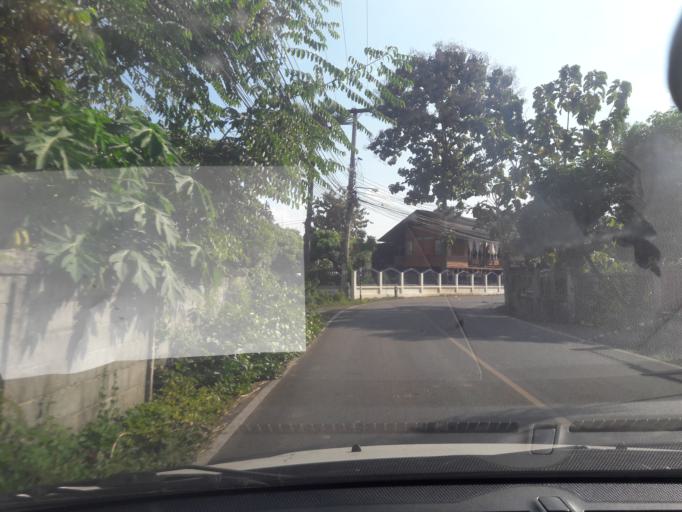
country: TH
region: Chiang Mai
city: San Kamphaeng
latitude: 18.7560
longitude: 99.1413
